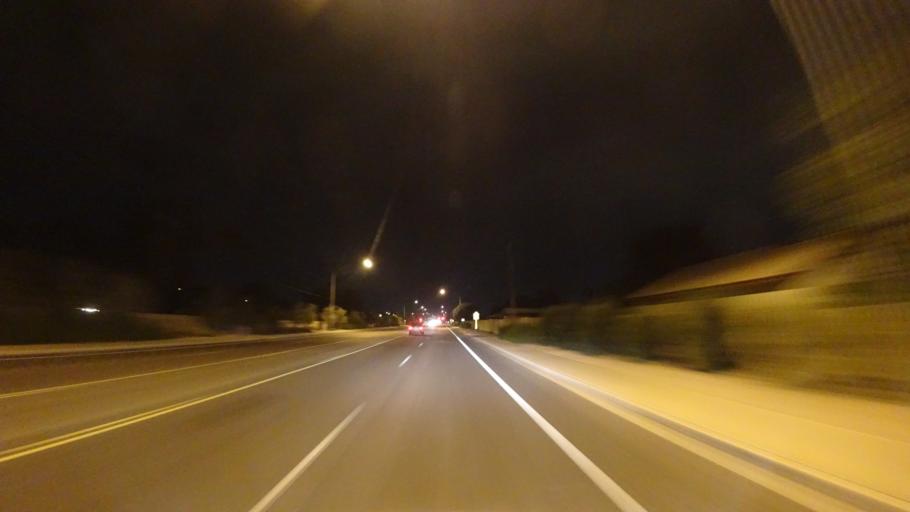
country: US
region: Arizona
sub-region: Maricopa County
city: Gilbert
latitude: 33.3977
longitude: -111.7713
